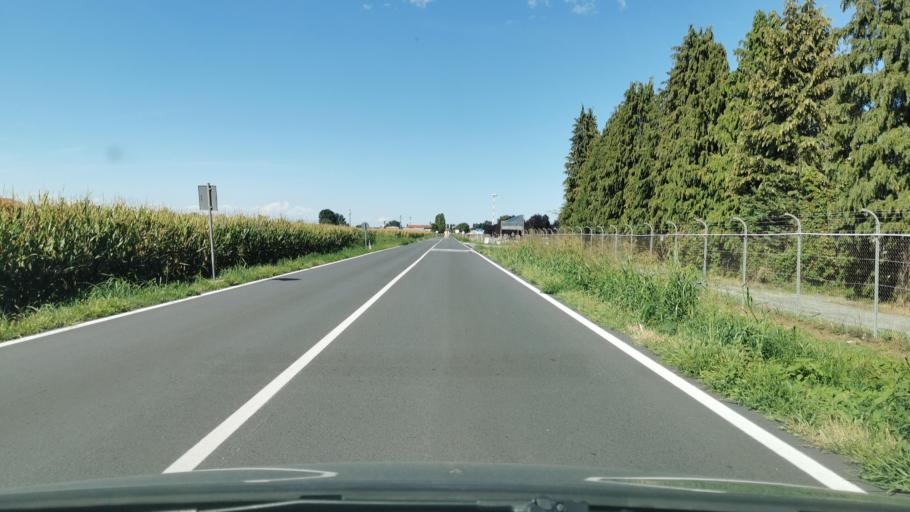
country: IT
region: Piedmont
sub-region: Provincia di Cuneo
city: Vottignasco
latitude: 44.5448
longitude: 7.6153
